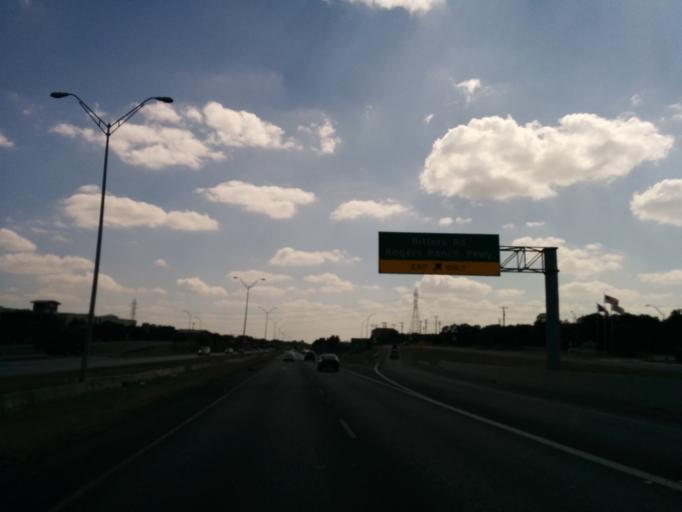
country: US
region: Texas
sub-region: Bexar County
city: Shavano Park
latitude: 29.6067
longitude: -98.5278
